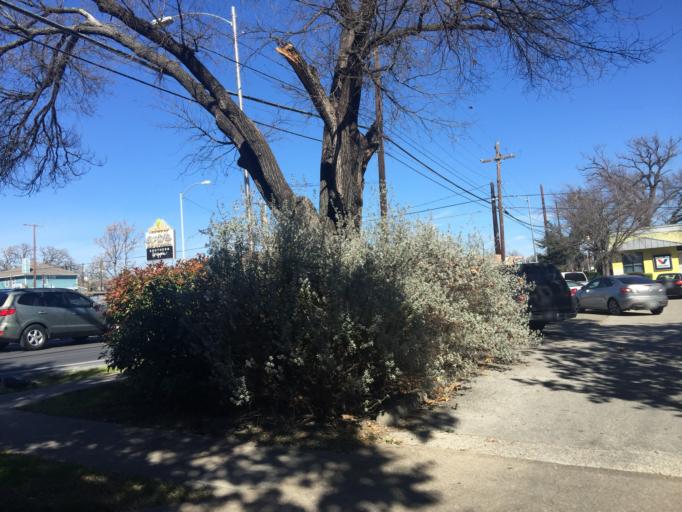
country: US
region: Texas
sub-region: Travis County
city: Austin
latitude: 30.3011
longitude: -97.7389
